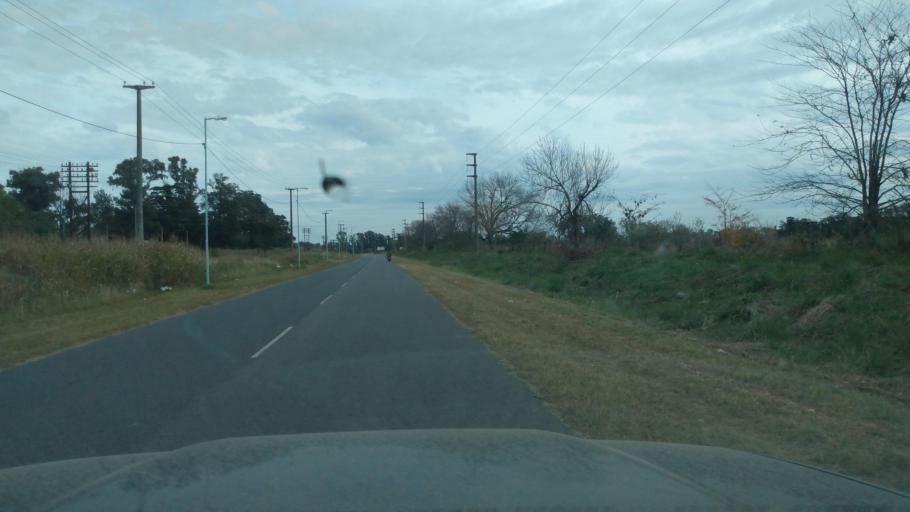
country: AR
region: Buenos Aires
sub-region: Partido de Lujan
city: Lujan
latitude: -34.5891
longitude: -59.1397
